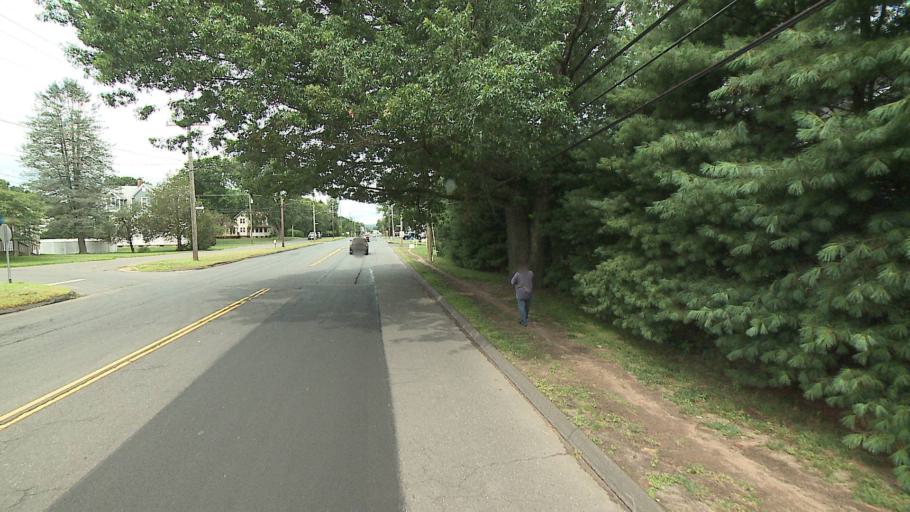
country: US
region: Connecticut
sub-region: Hartford County
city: Plainville
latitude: 41.6692
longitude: -72.8480
